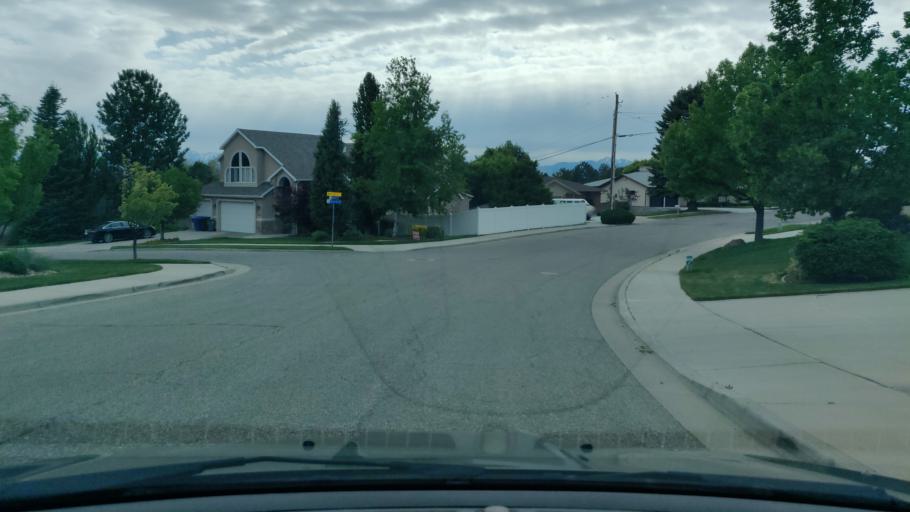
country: US
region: Utah
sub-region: Salt Lake County
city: Cottonwood Heights
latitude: 40.6071
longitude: -111.8155
